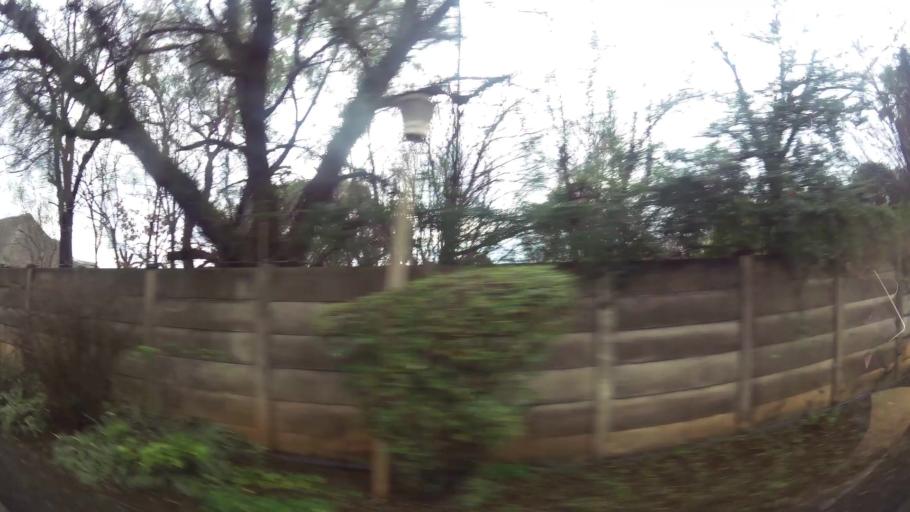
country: ZA
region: Gauteng
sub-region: Sedibeng District Municipality
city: Vereeniging
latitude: -26.6481
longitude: 27.9737
